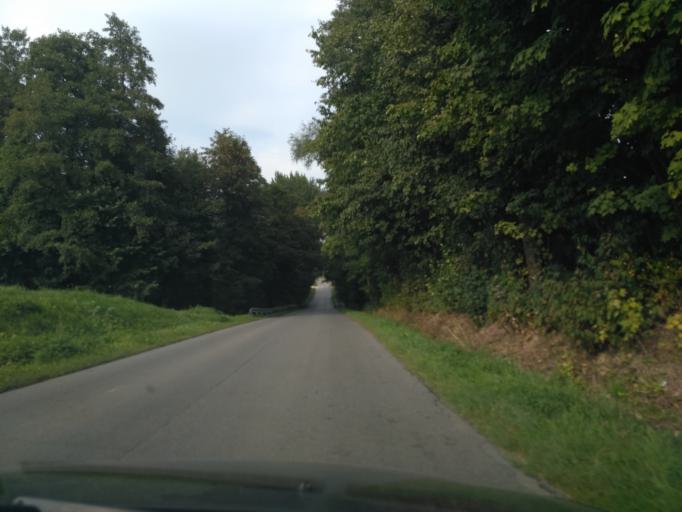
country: PL
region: Subcarpathian Voivodeship
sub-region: Powiat rzeszowski
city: Trzciana
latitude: 50.0513
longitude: 21.8319
